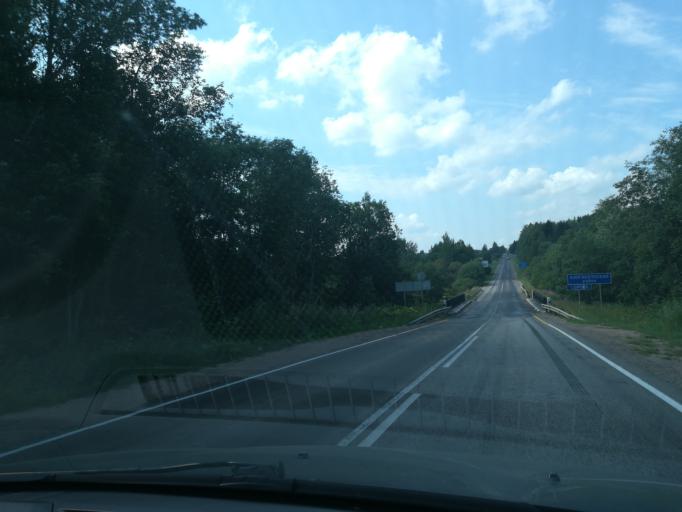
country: RU
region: Leningrad
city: Kopor'ye
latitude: 59.6367
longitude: 28.9840
